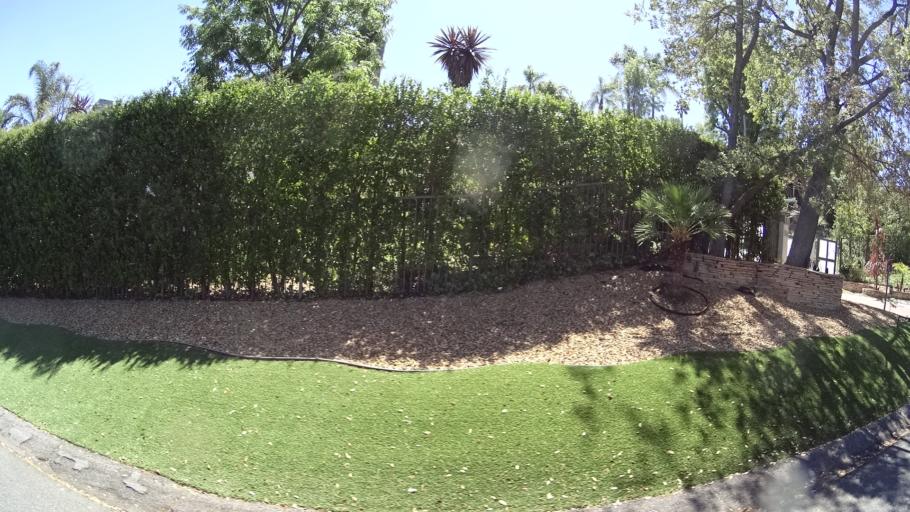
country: US
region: California
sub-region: Ventura County
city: Thousand Oaks
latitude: 34.1916
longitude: -118.8537
